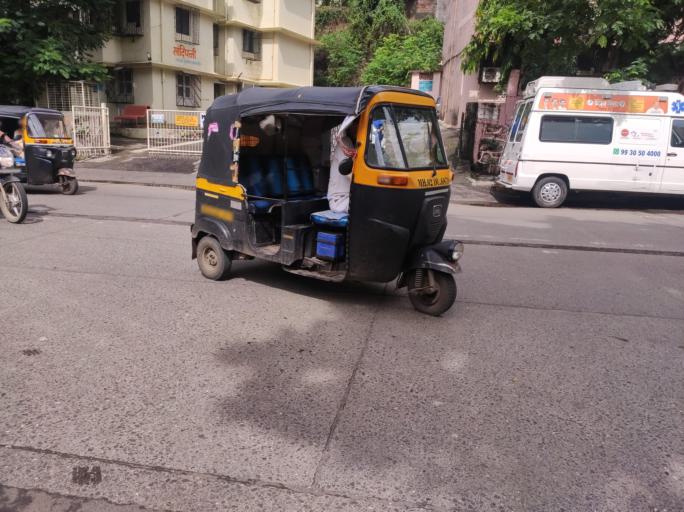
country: IN
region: Maharashtra
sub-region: Mumbai Suburban
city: Borivli
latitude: 19.2471
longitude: 72.8544
